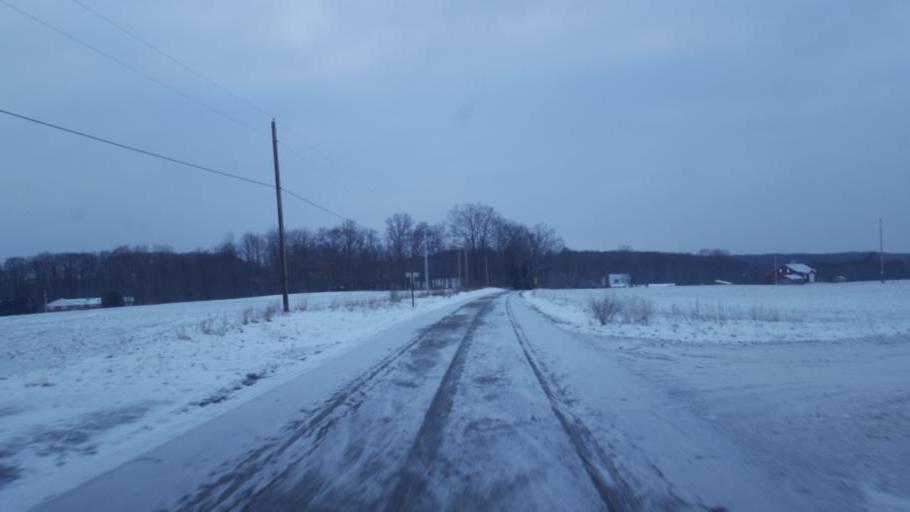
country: US
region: Pennsylvania
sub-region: Venango County
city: Sugarcreek
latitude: 41.4345
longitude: -79.9775
